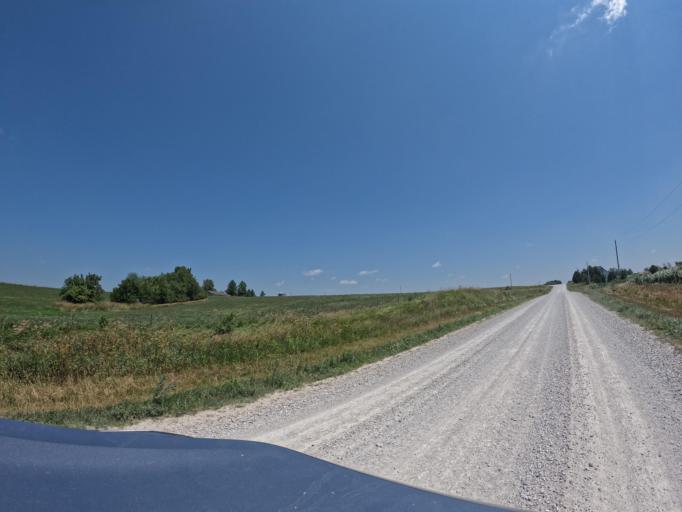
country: US
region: Iowa
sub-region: Keokuk County
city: Sigourney
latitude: 41.2579
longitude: -92.1719
